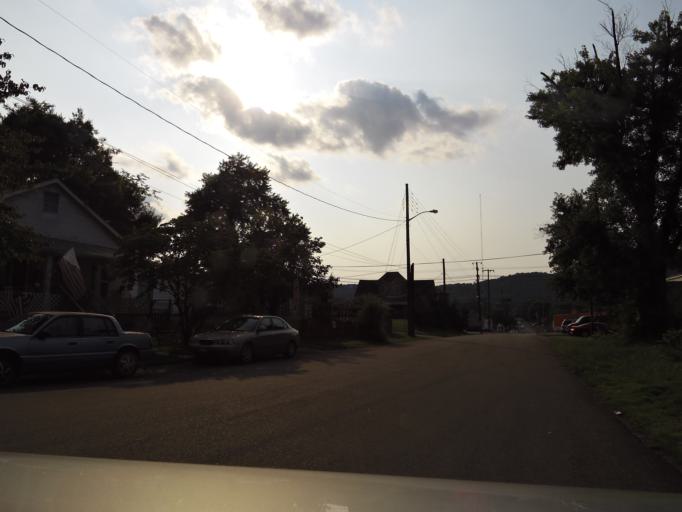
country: US
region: Tennessee
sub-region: Knox County
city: Knoxville
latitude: 35.9809
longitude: -83.9499
